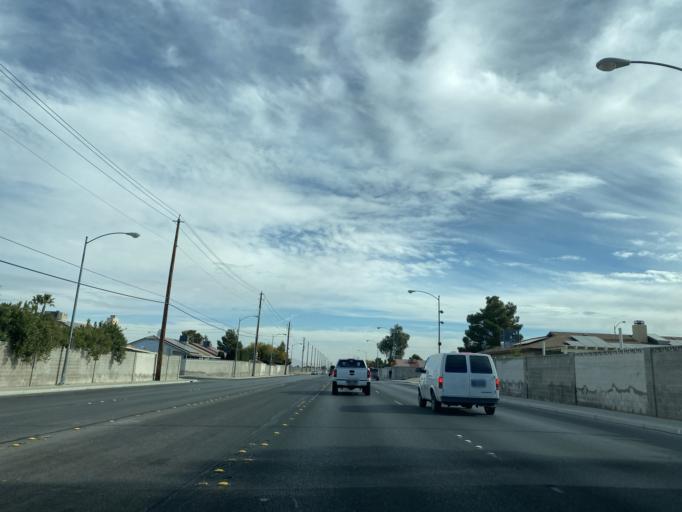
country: US
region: Nevada
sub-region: Clark County
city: Las Vegas
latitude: 36.2467
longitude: -115.2008
